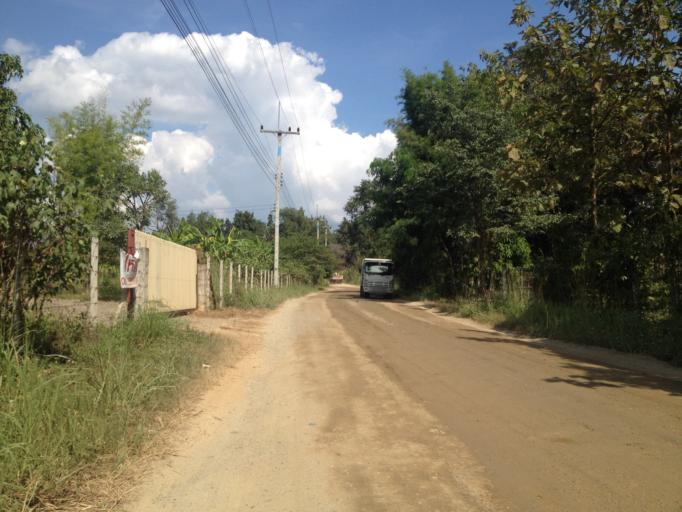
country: TH
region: Chiang Mai
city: Hang Dong
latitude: 18.6969
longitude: 98.8726
